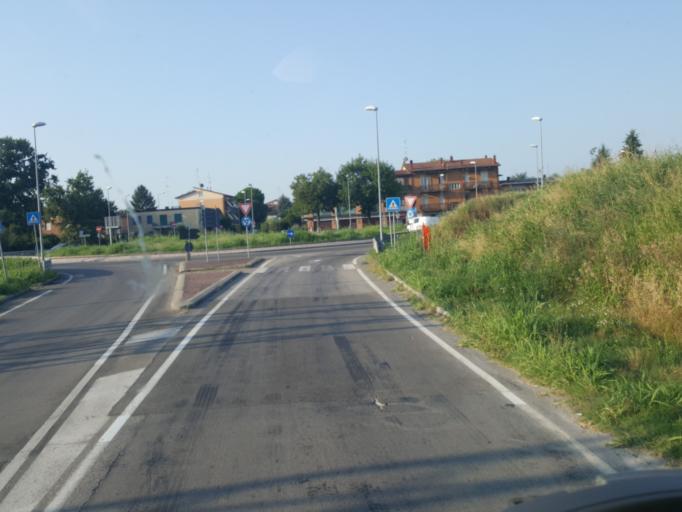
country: IT
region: Emilia-Romagna
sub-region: Provincia di Modena
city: Spilamberto
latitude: 44.5362
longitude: 11.0141
